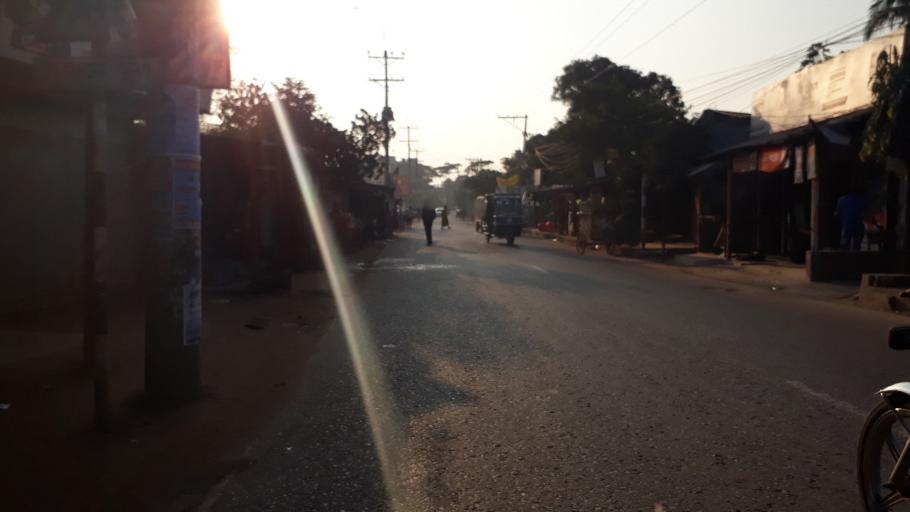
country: BD
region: Dhaka
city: Tungi
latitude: 23.8789
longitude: 90.2944
